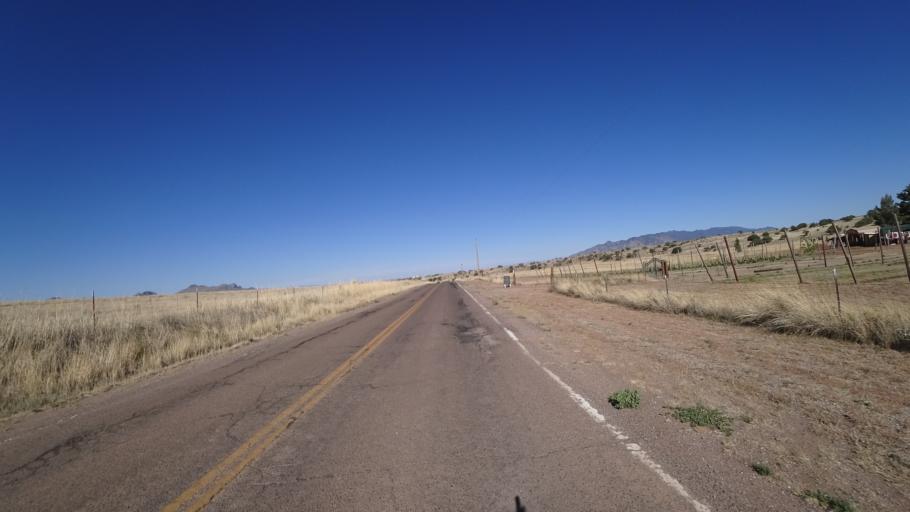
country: US
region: Arizona
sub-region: Cochise County
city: Huachuca City
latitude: 31.6080
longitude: -110.5828
